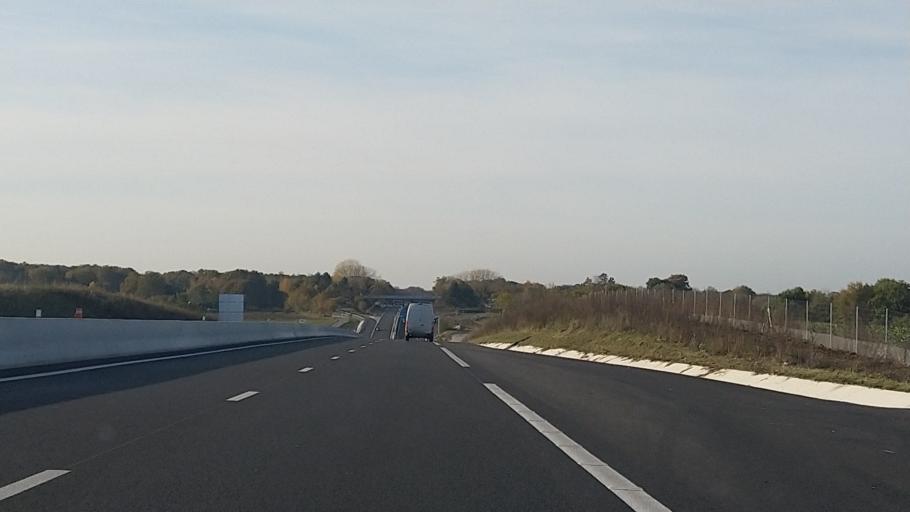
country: FR
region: Ile-de-France
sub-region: Departement du Val-d'Oise
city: Maffliers
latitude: 49.0986
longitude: 2.2892
